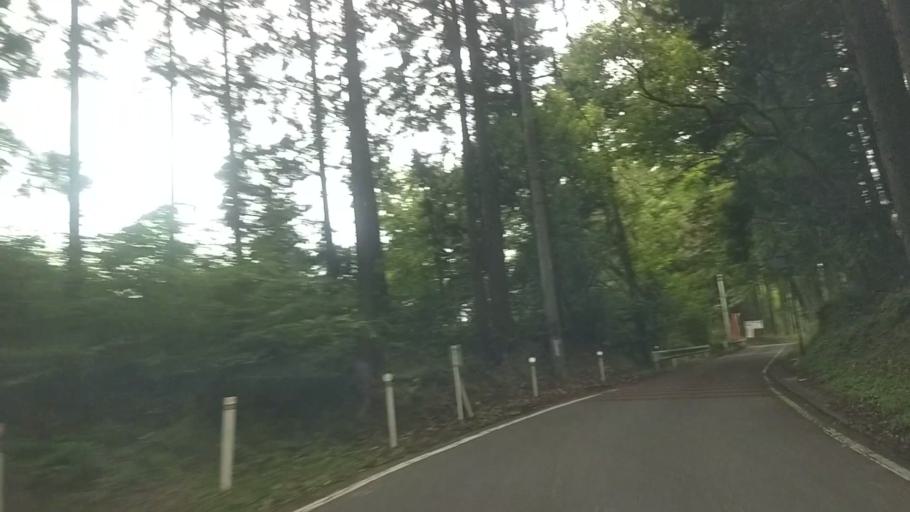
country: JP
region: Chiba
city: Kawaguchi
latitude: 35.1900
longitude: 140.1381
